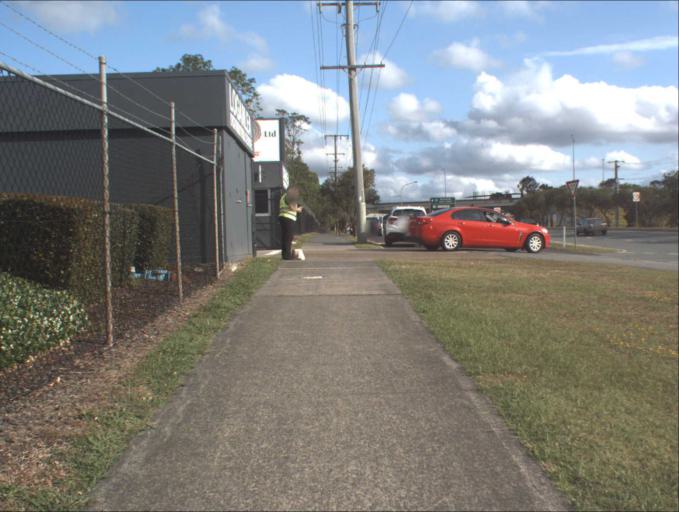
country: AU
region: Queensland
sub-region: Logan
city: Waterford West
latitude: -27.6669
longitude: 153.1212
